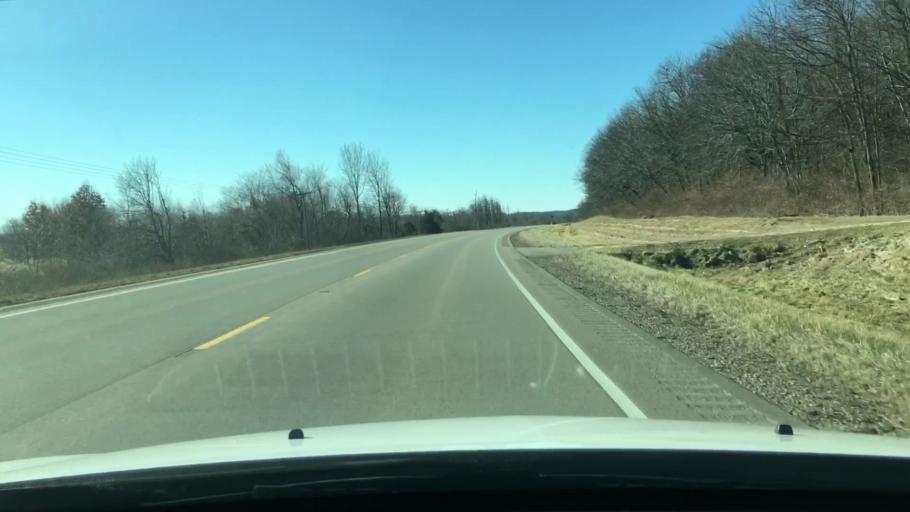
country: US
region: Illinois
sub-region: Peoria County
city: Glasford
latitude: 40.5229
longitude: -89.8835
